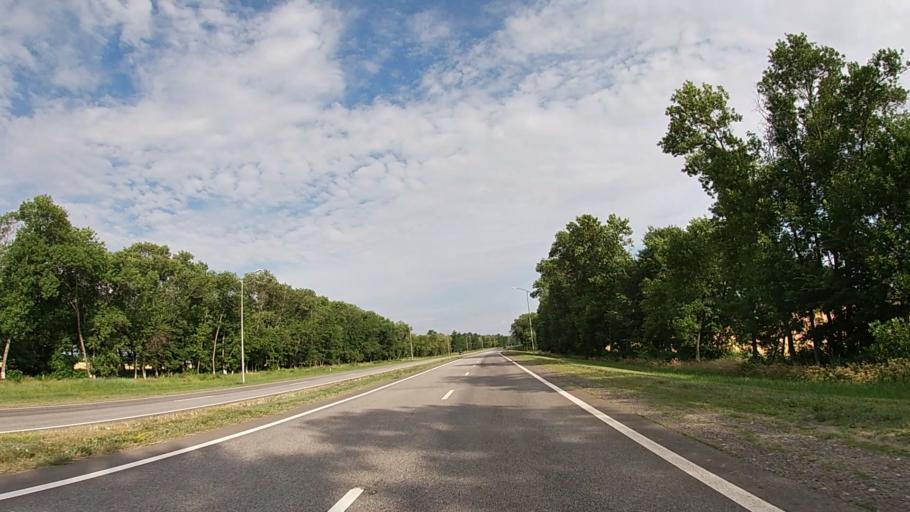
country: RU
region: Belgorod
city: Tomarovka
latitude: 50.6714
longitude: 36.3009
